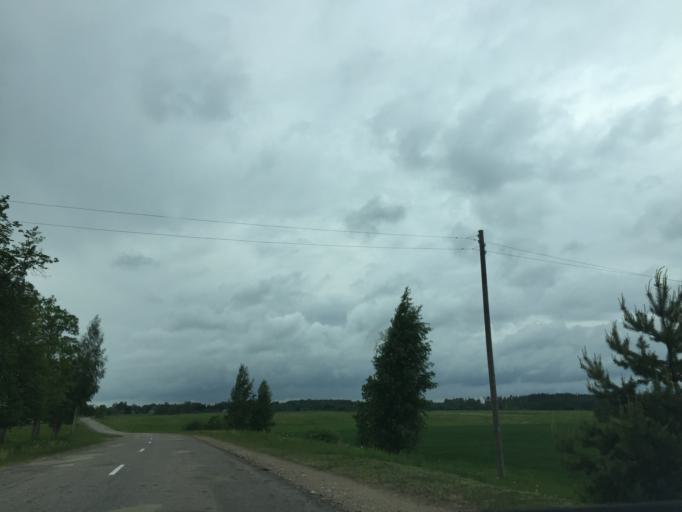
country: LV
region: Varkava
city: Vecvarkava
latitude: 56.1025
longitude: 26.5162
